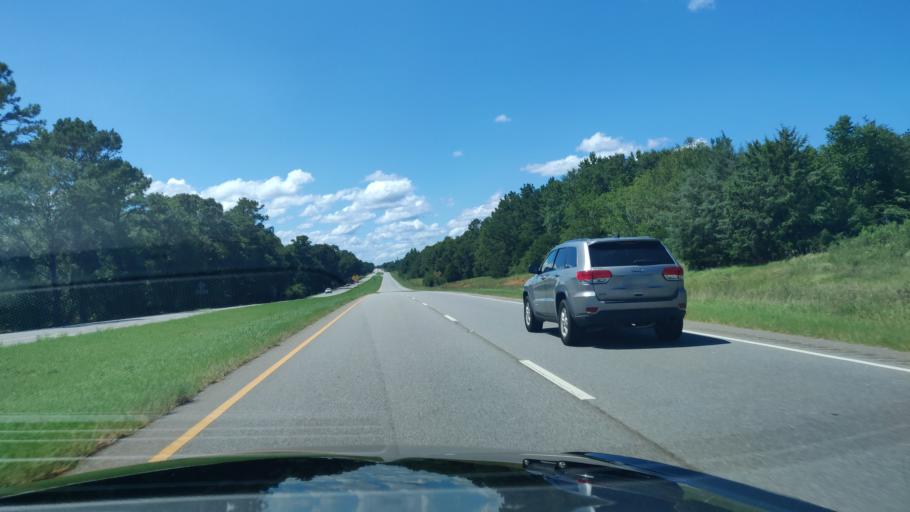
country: US
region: Georgia
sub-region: Terrell County
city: Dawson
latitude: 31.8778
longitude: -84.4987
